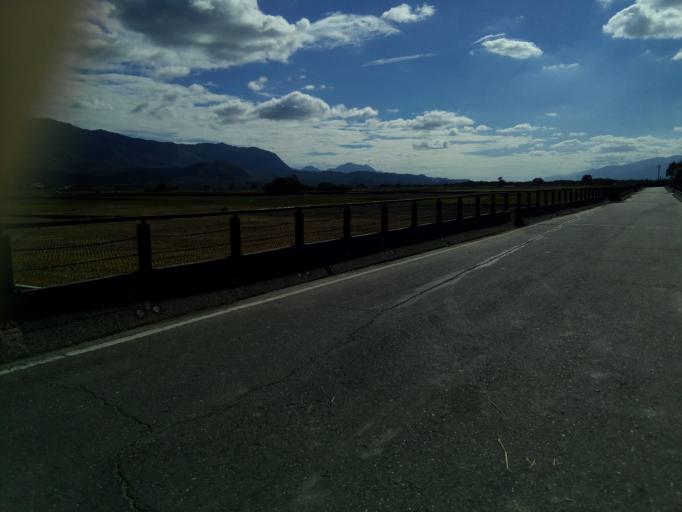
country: TW
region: Taiwan
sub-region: Taitung
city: Taitung
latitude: 23.1030
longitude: 121.2071
